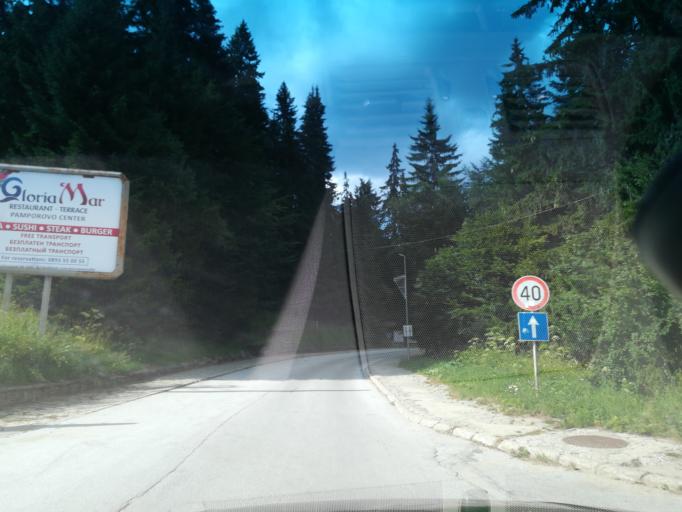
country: BG
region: Smolyan
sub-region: Obshtina Smolyan
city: Smolyan
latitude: 41.6540
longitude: 24.6938
